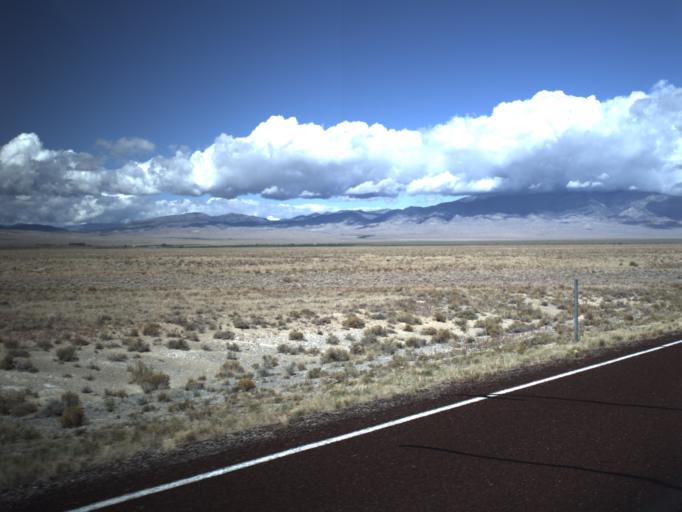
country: US
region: Nevada
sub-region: White Pine County
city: McGill
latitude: 38.9744
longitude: -114.0340
